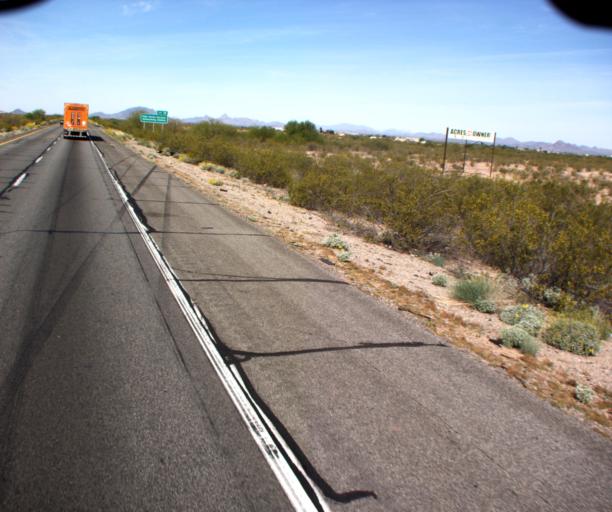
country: US
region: Arizona
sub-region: Maricopa County
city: Buckeye
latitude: 33.4782
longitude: -112.8502
